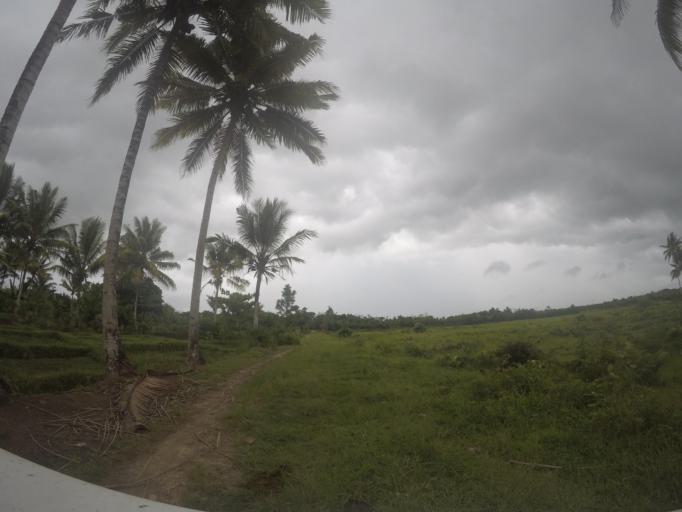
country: TL
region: Lautem
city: Lospalos
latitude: -8.5163
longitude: 126.9914
